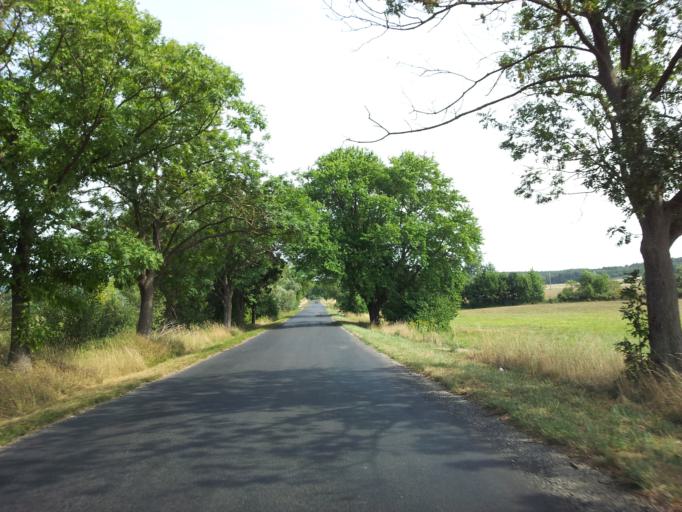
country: HU
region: Veszprem
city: Revfueloep
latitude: 46.8512
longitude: 17.5789
